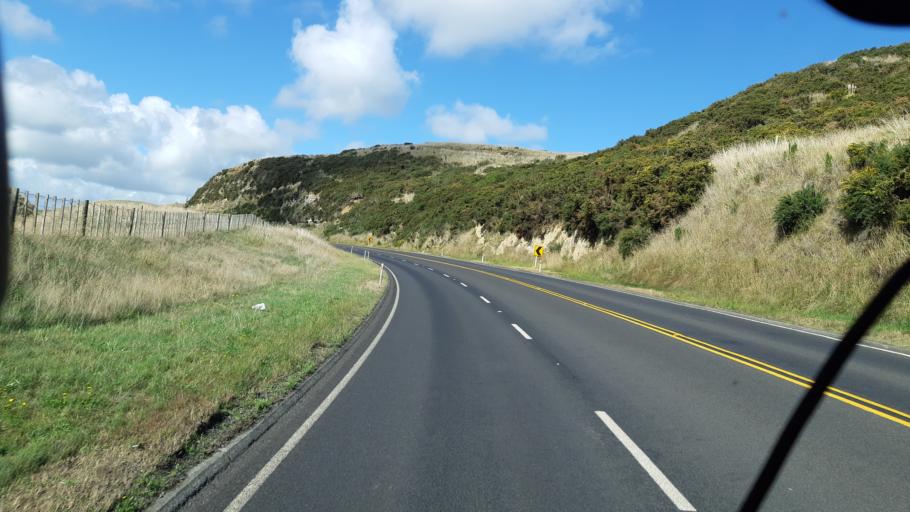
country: NZ
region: Manawatu-Wanganui
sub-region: Wanganui District
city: Wanganui
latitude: -40.0229
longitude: 175.1794
